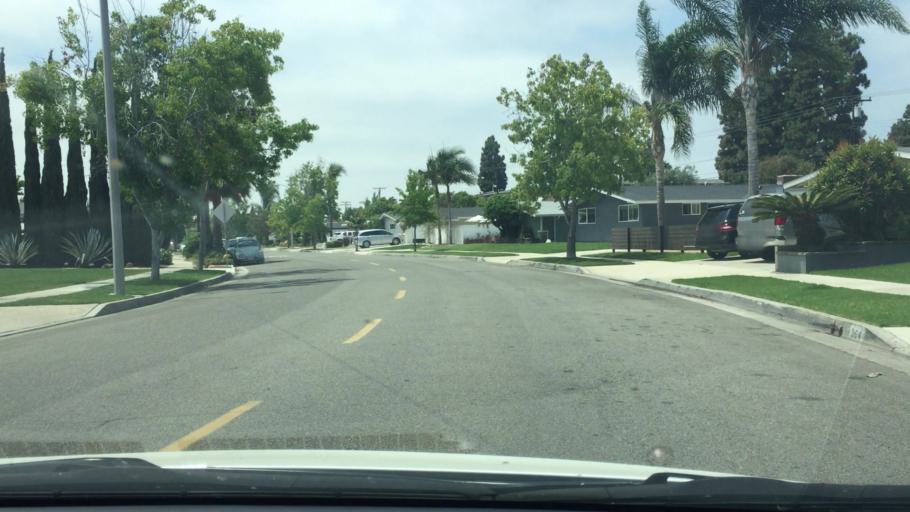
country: US
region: California
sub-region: Orange County
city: Costa Mesa
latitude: 33.6668
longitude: -117.9150
